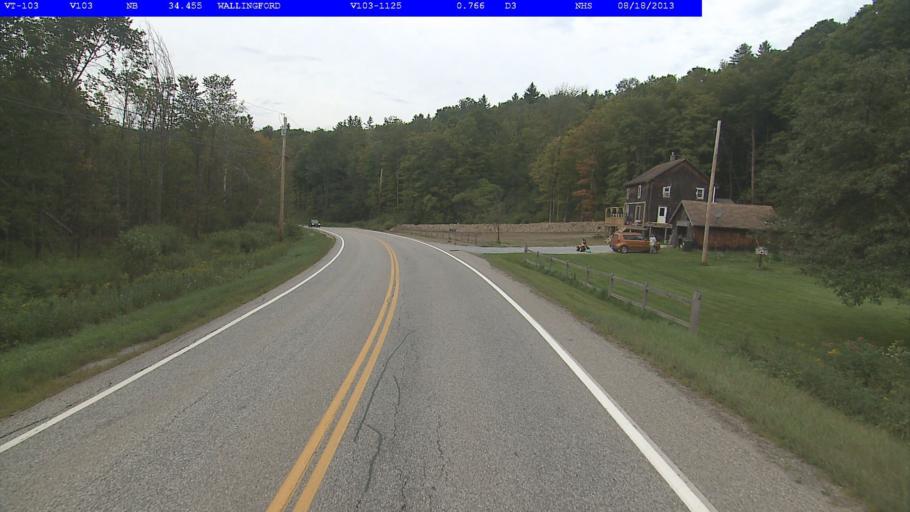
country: US
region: Vermont
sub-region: Rutland County
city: Rutland
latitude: 43.4577
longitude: -72.8783
